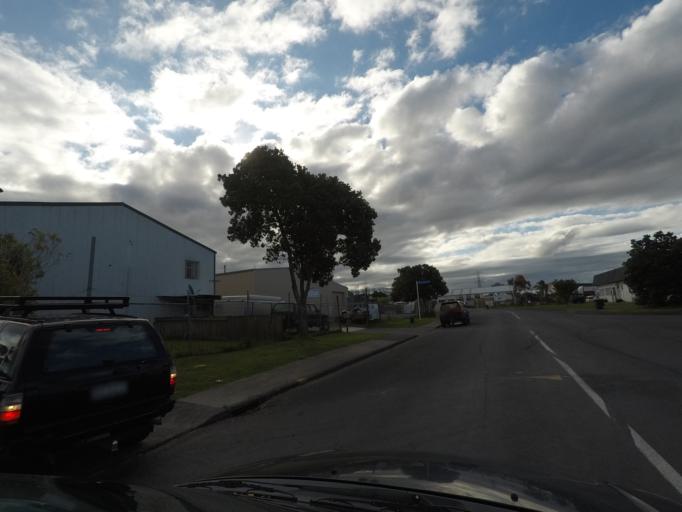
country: NZ
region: Auckland
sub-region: Auckland
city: Rosebank
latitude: -36.8867
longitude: 174.6636
